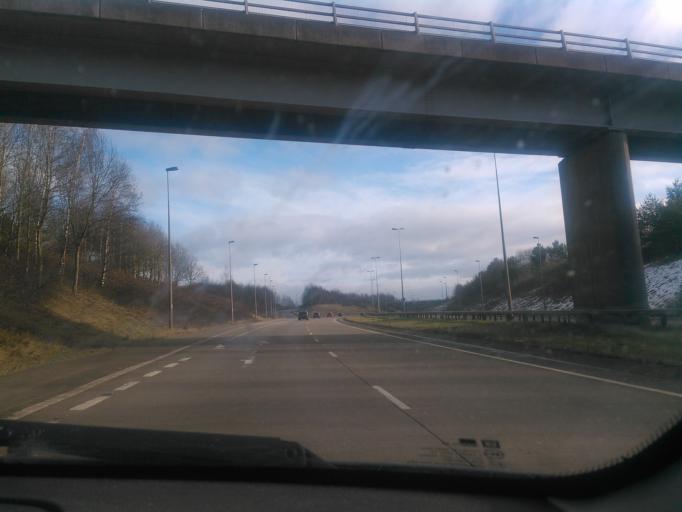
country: GB
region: England
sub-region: Staffordshire
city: Uttoxeter
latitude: 52.9103
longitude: -1.8296
